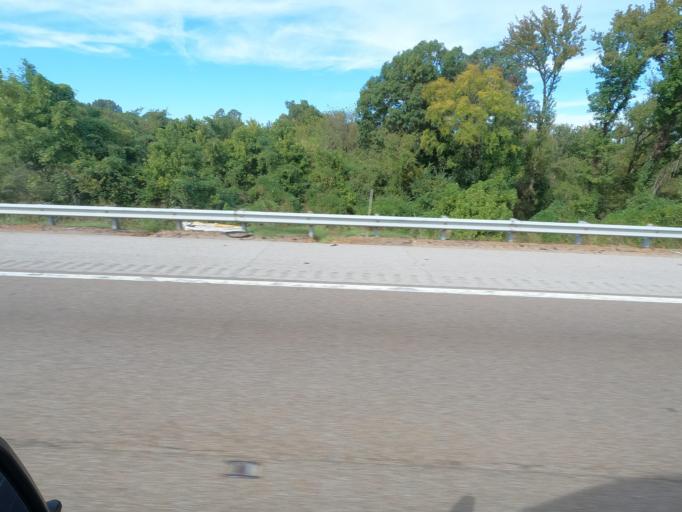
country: US
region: Tennessee
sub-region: Shelby County
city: Arlington
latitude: 35.2767
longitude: -89.6376
